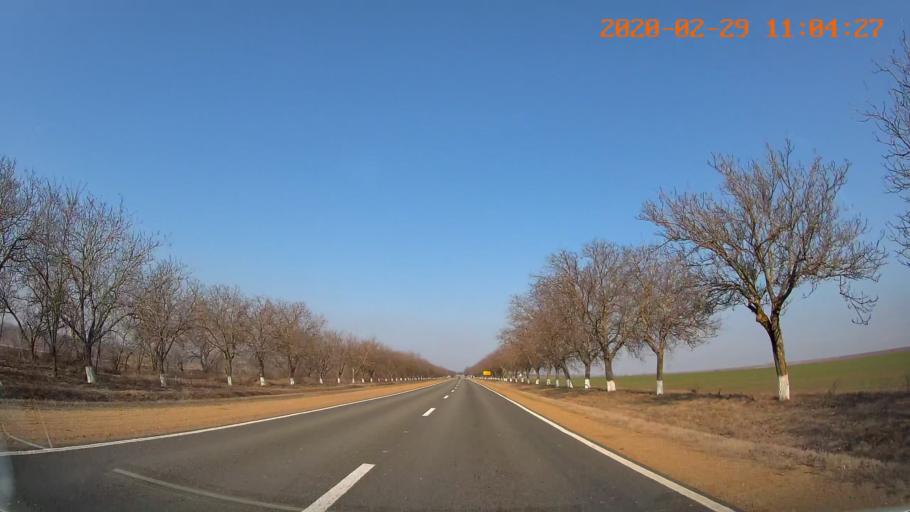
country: MD
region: Criuleni
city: Criuleni
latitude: 47.1893
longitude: 29.2022
